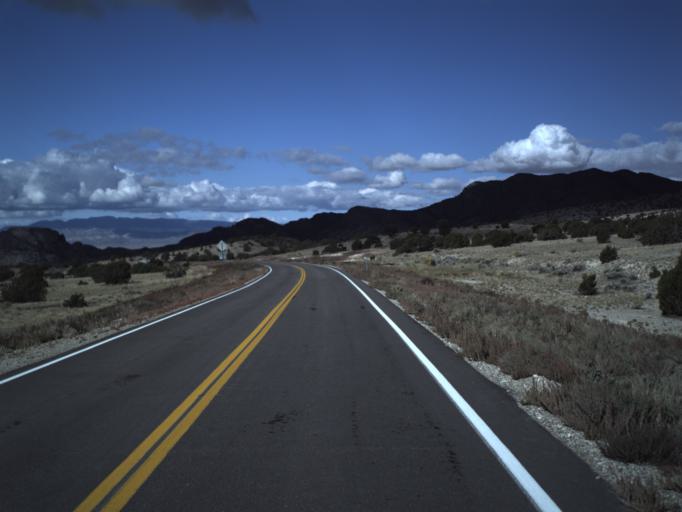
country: US
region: Utah
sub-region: Beaver County
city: Milford
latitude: 38.5174
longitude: -113.5461
